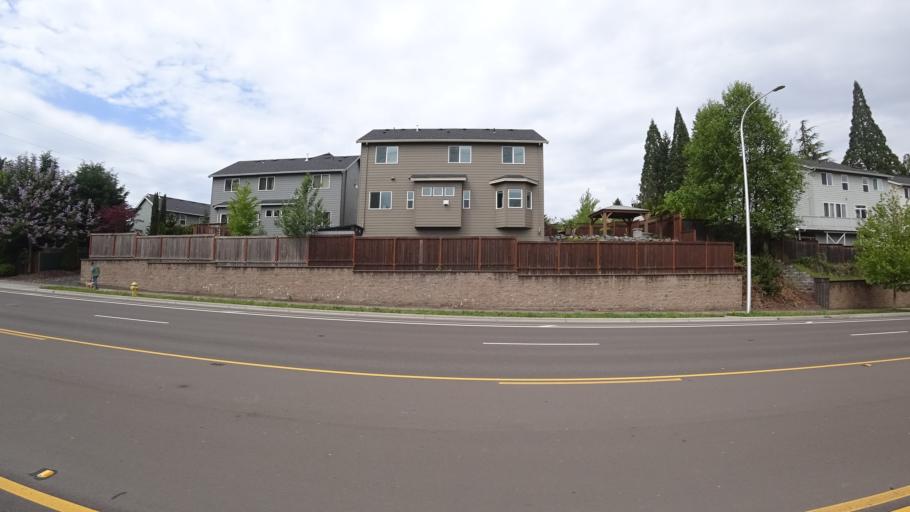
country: US
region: Oregon
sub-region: Washington County
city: Rockcreek
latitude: 45.5199
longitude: -122.9246
